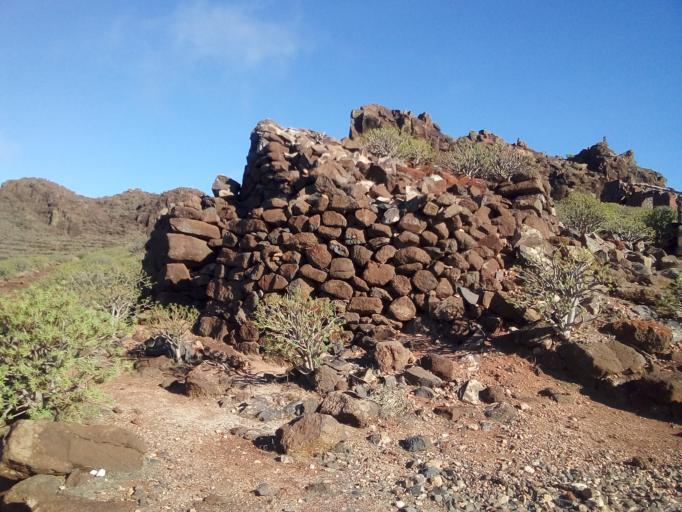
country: ES
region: Canary Islands
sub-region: Provincia de Santa Cruz de Tenerife
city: Vallehermosa
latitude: 28.1126
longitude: -17.3360
